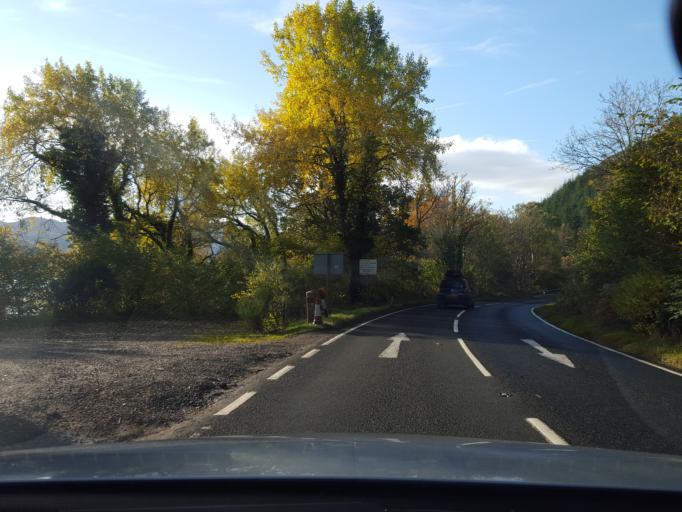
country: GB
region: Scotland
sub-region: Highland
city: Beauly
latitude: 57.2360
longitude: -4.5576
